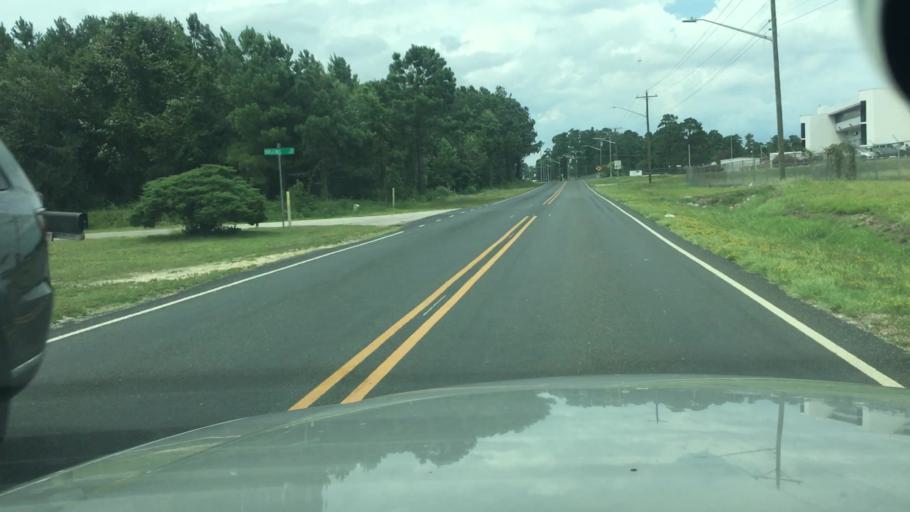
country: US
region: North Carolina
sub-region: Cumberland County
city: Hope Mills
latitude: 34.9884
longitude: -78.8905
